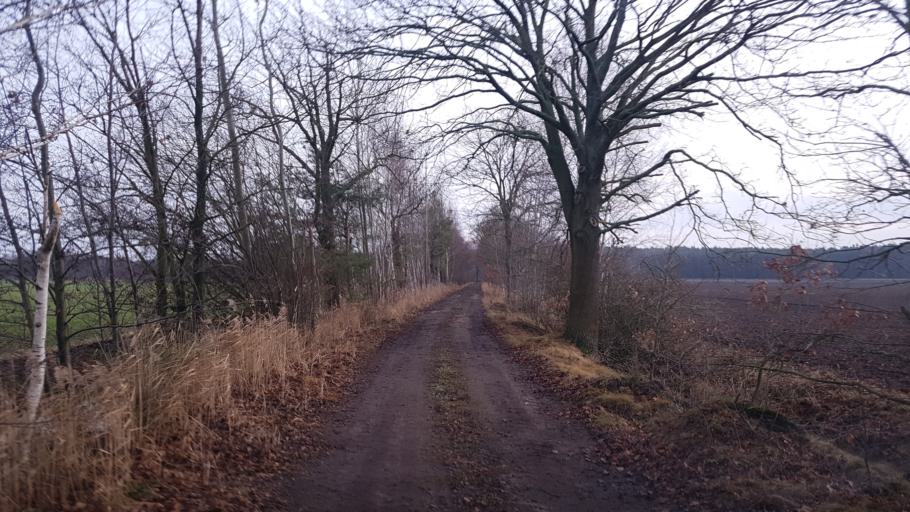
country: DE
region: Brandenburg
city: Ruckersdorf
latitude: 51.5909
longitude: 13.6167
